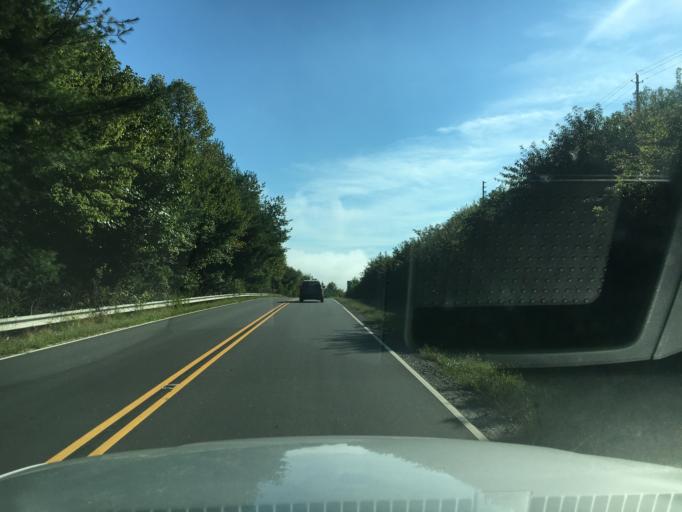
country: US
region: North Carolina
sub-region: Haywood County
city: Lake Junaluska
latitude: 35.5253
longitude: -82.9534
